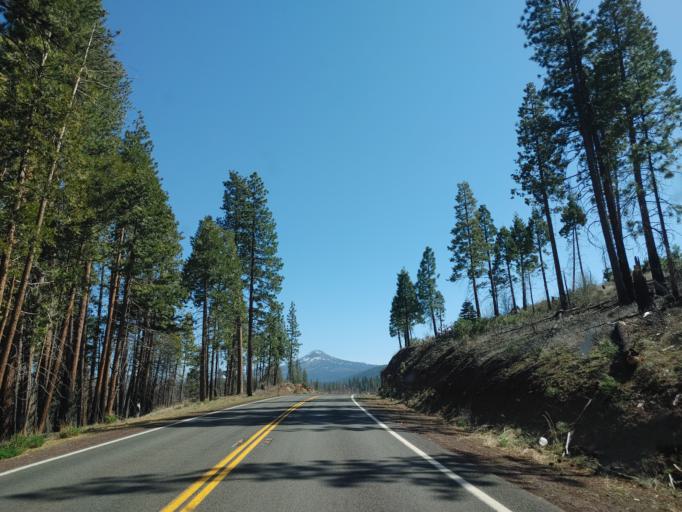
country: US
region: California
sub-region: Shasta County
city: Burney
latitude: 40.7926
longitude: -121.5071
